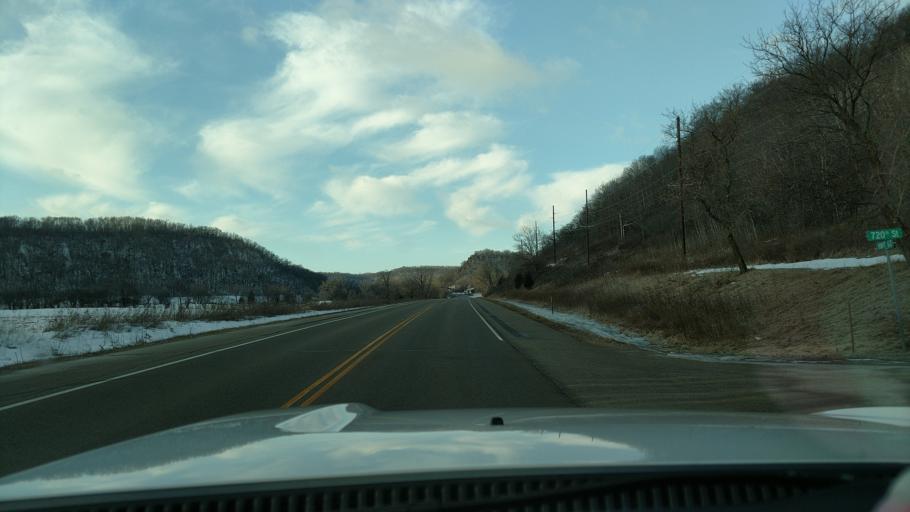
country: US
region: Minnesota
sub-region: Wabasha County
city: Lake City
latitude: 44.4249
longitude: -92.2941
